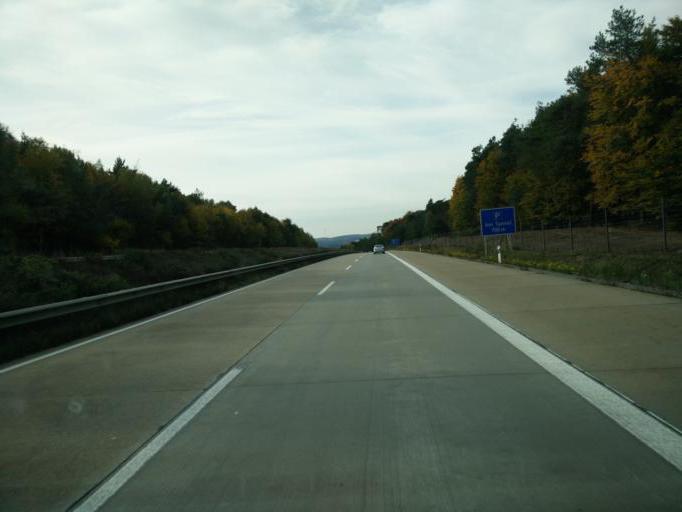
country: DE
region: Rheinland-Pfalz
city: Enkenbach-Alsenborn
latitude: 49.4800
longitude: 7.9269
